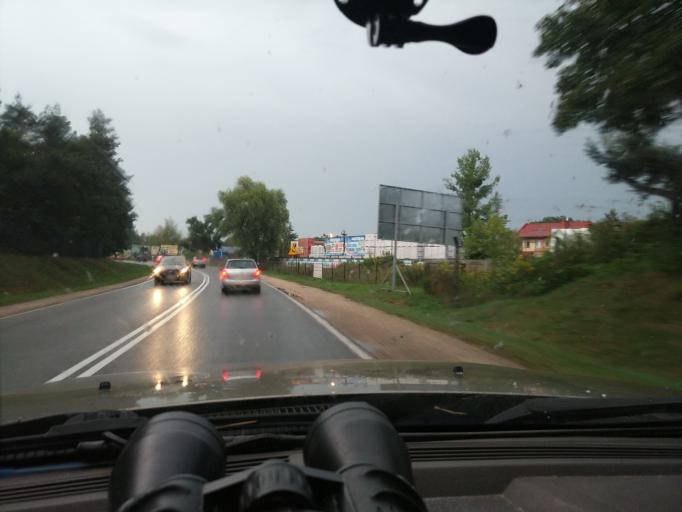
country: PL
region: Masovian Voivodeship
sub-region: Powiat pruszkowski
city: Granica
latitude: 52.1470
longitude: 20.7892
